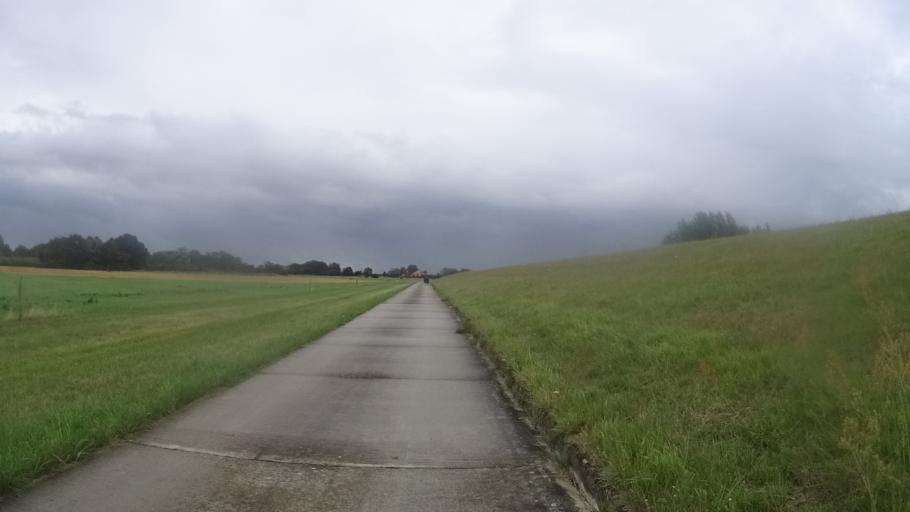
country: DE
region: Lower Saxony
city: Neu Darchau
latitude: 53.2583
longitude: 10.8438
